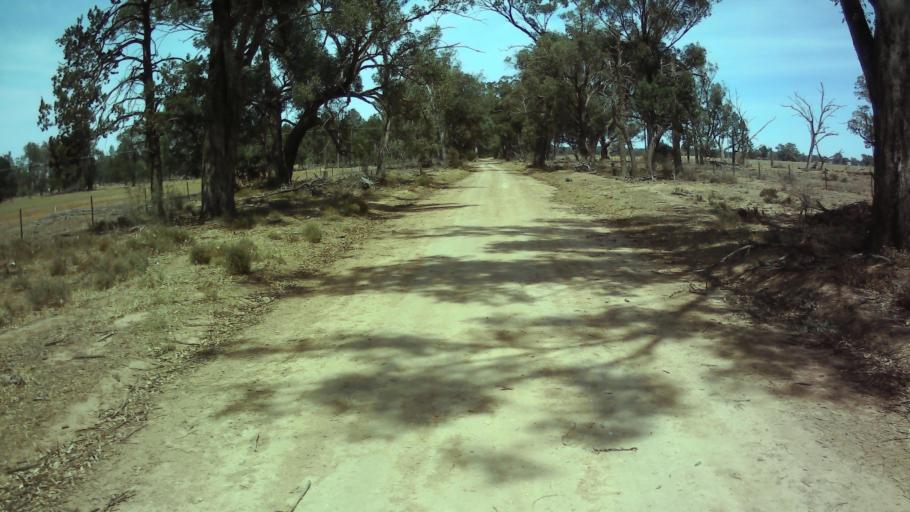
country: AU
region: New South Wales
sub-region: Weddin
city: Grenfell
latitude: -34.0297
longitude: 147.9372
